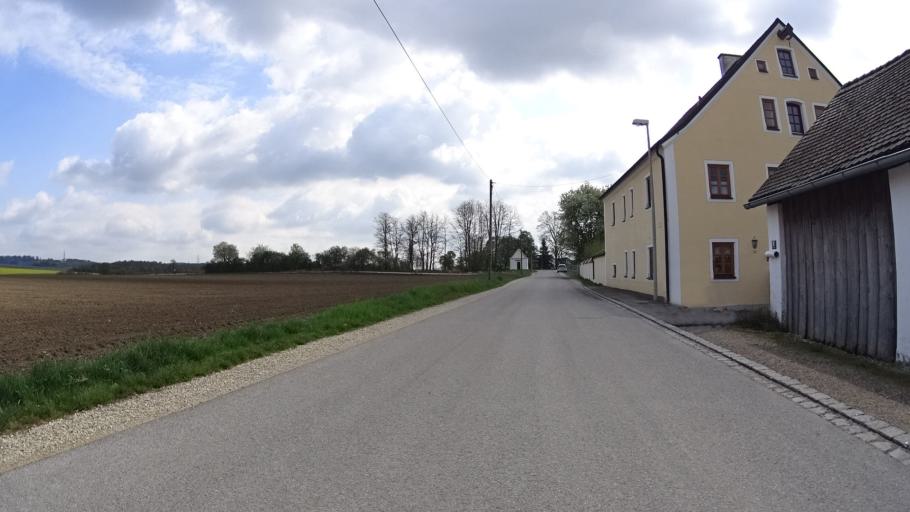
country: DE
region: Bavaria
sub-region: Upper Bavaria
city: Wettstetten
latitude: 48.8276
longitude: 11.3874
